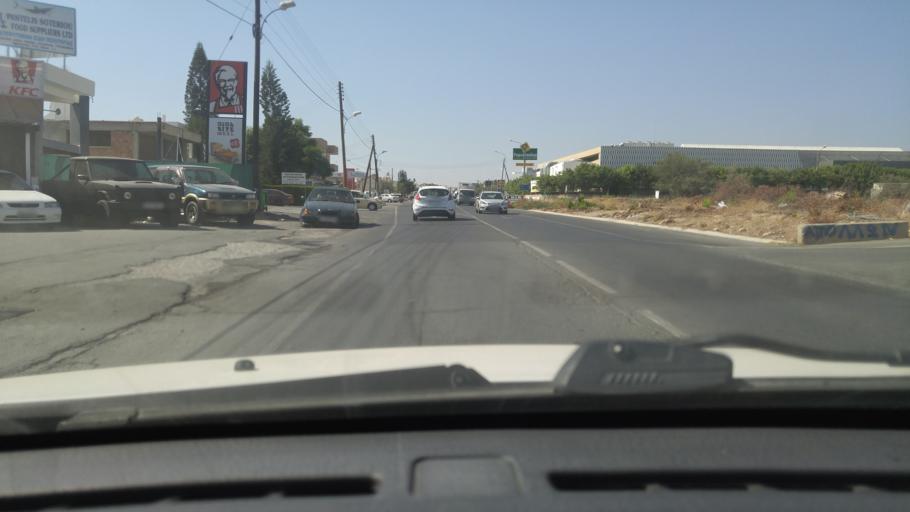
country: CY
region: Limassol
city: Ypsonas
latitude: 34.6819
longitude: 32.9738
